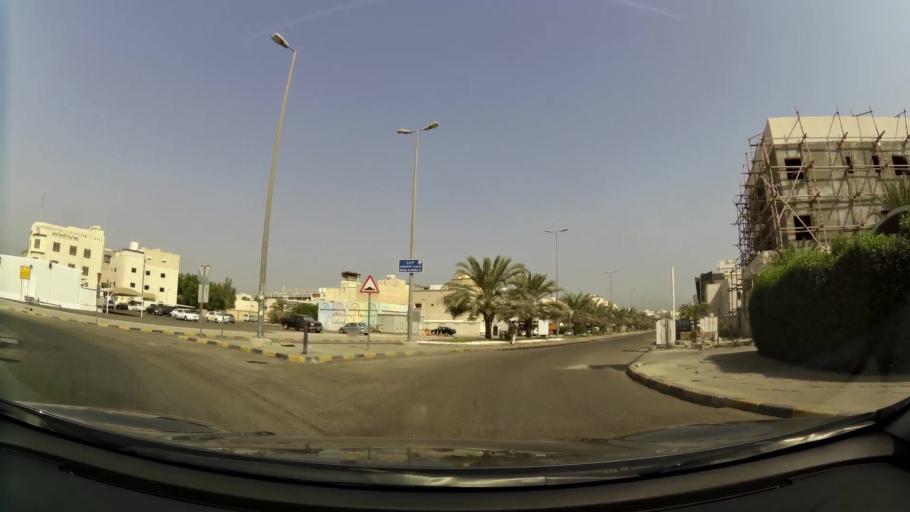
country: KW
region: Al Asimah
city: Ad Dasmah
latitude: 29.3518
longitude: 48.0032
